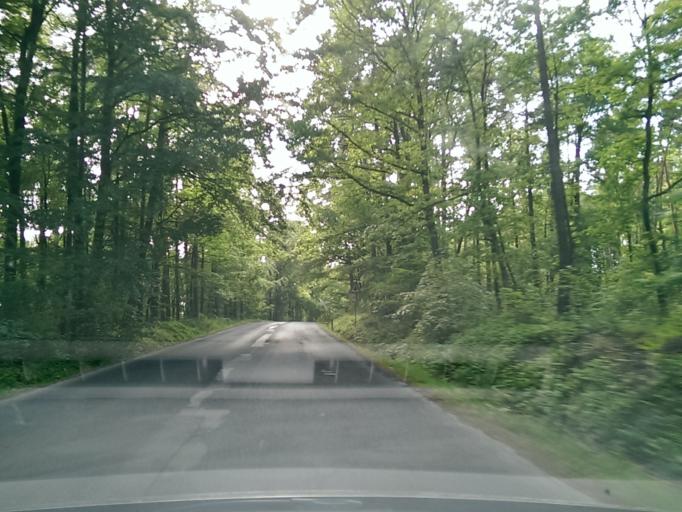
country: CZ
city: Duba
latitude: 50.5546
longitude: 14.5909
